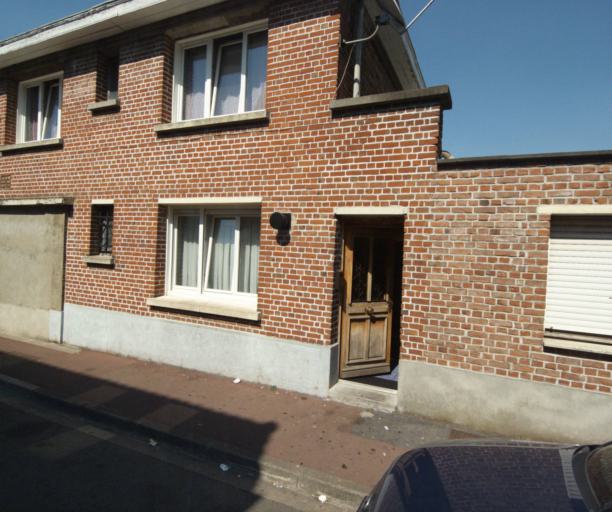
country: FR
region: Nord-Pas-de-Calais
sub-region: Departement du Nord
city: Tourcoing
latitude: 50.7152
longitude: 3.1709
